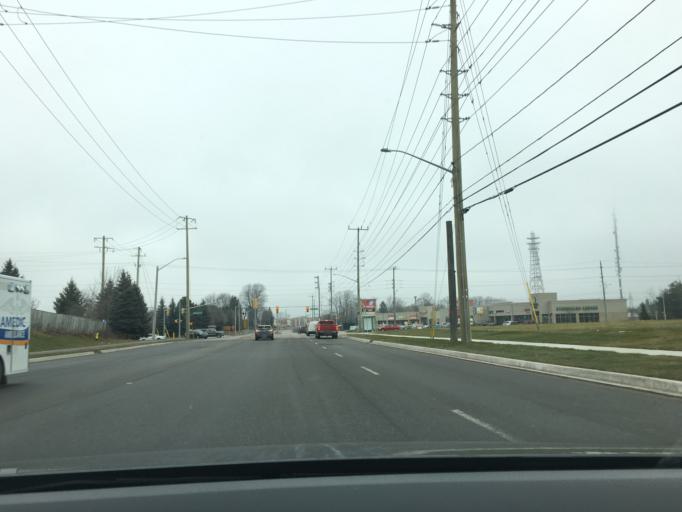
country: CA
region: Ontario
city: Barrie
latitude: 44.3458
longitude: -79.7049
